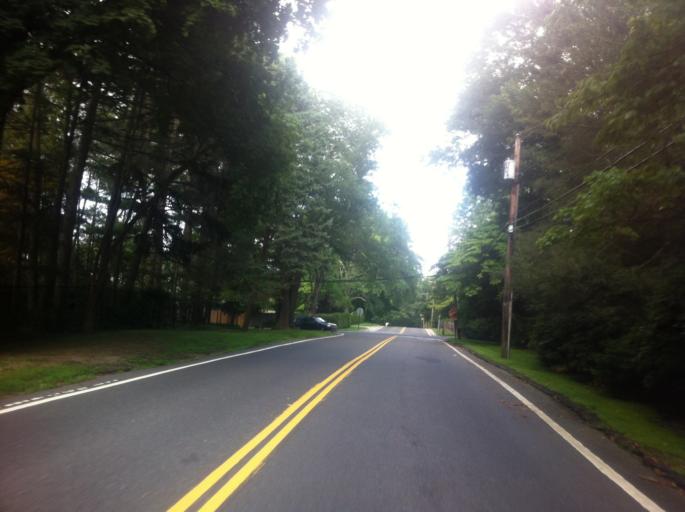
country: US
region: New York
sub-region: Nassau County
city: Glen Head
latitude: 40.8522
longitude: -73.6138
